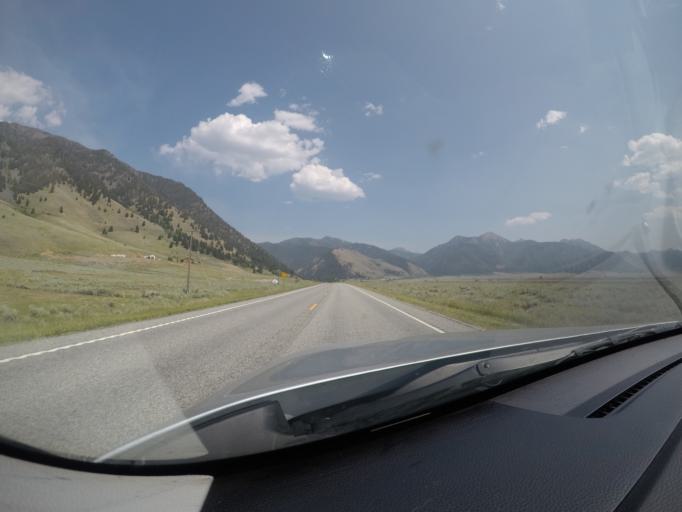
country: US
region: Montana
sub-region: Gallatin County
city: West Yellowstone
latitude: 44.8285
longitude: -111.4705
